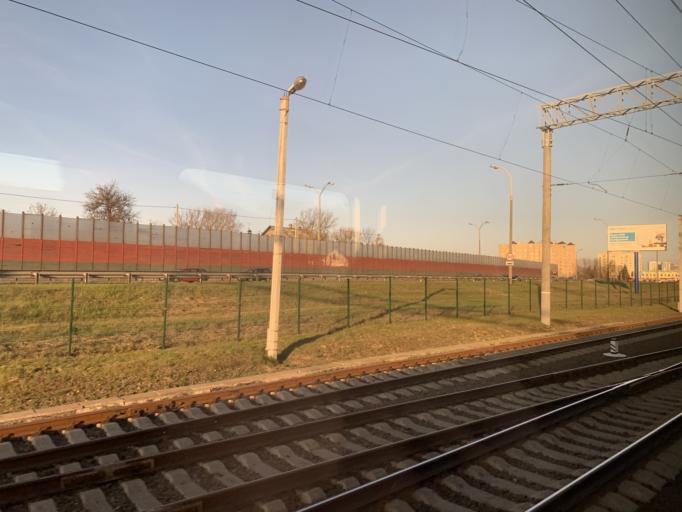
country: BY
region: Minsk
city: Zhdanovichy
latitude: 53.9492
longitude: 27.4202
